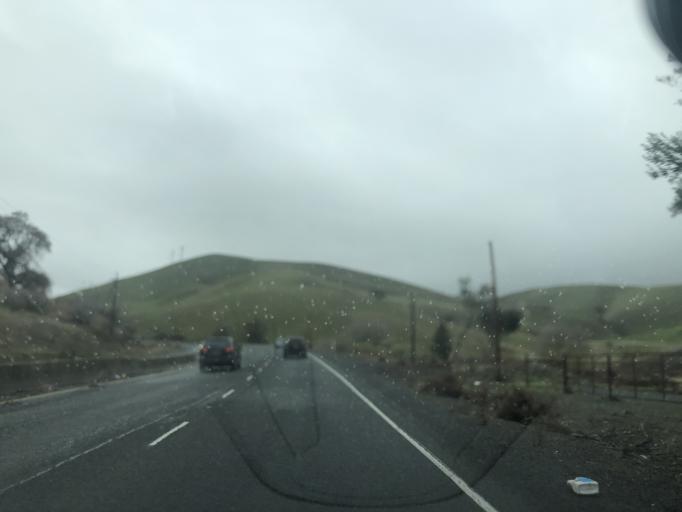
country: US
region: California
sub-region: Contra Costa County
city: Clayton
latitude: 37.9748
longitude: -121.9123
